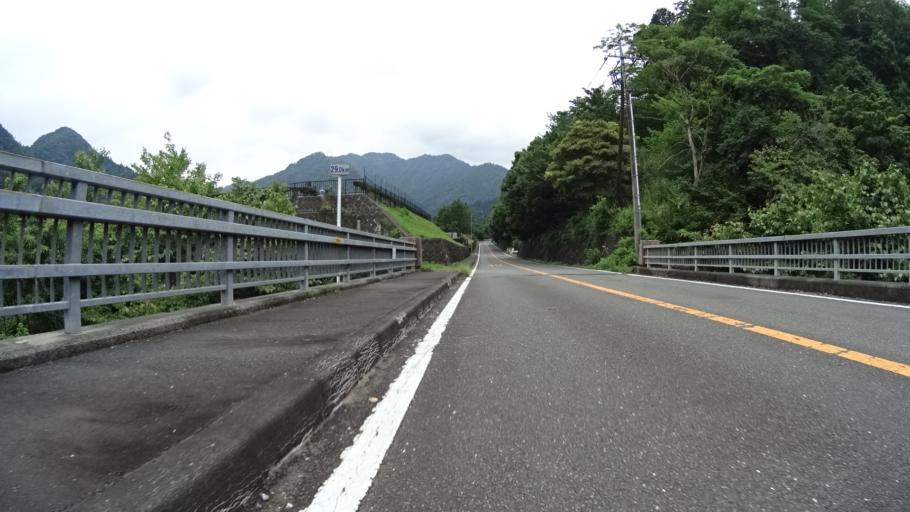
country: JP
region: Kanagawa
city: Hadano
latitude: 35.5094
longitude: 139.2312
